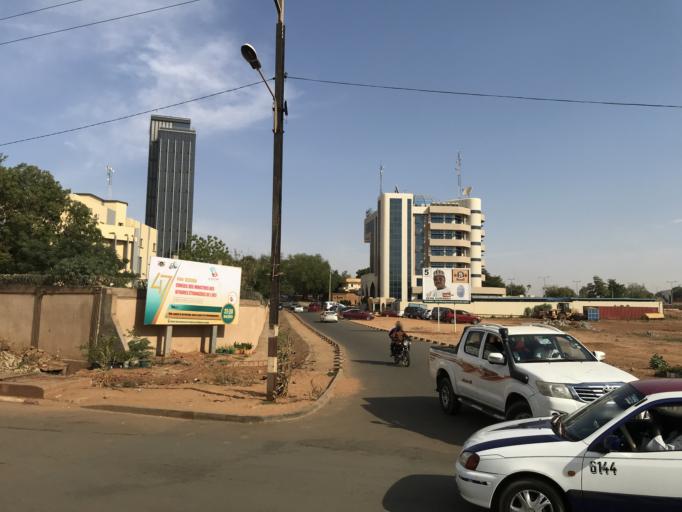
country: NE
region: Niamey
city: Niamey
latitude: 13.5153
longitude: 2.1068
